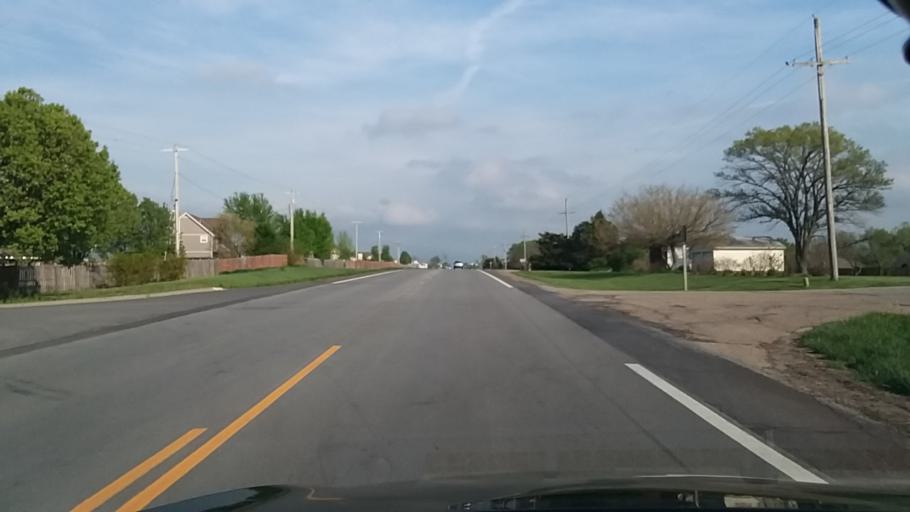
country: US
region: Kansas
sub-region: Douglas County
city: Baldwin City
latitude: 38.7777
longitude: -95.1719
